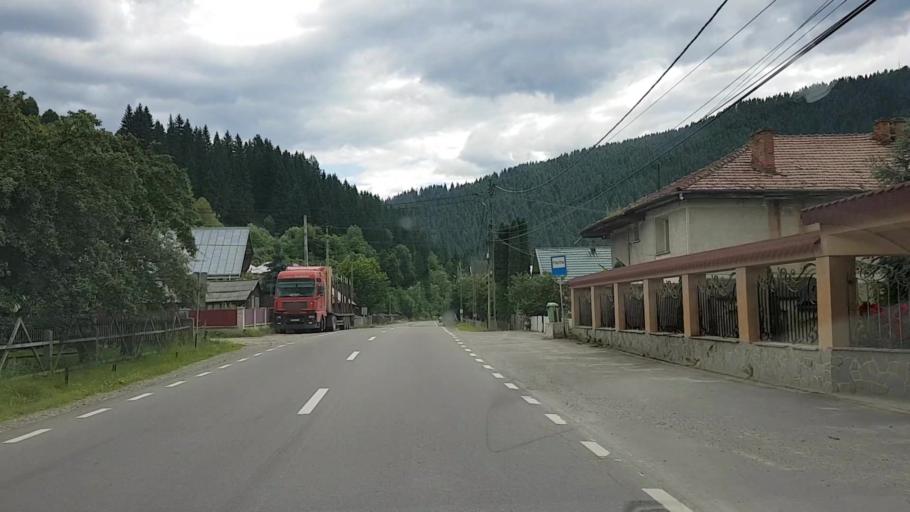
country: RO
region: Neamt
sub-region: Comuna Farcasa
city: Farcasa
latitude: 47.1551
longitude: 25.8410
